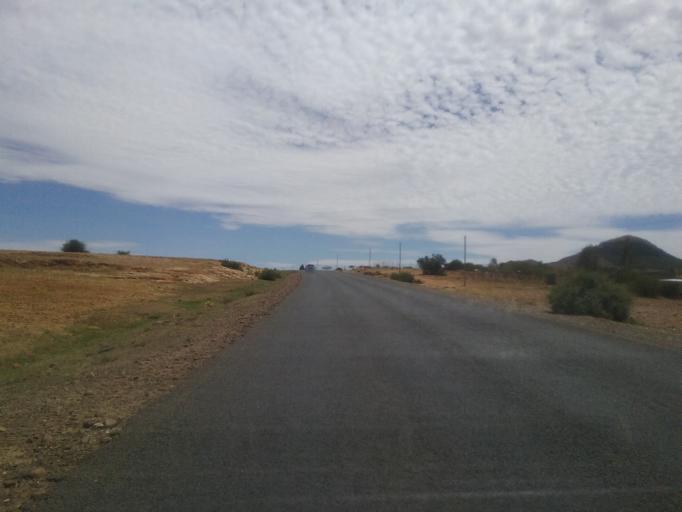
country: LS
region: Mafeteng
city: Mafeteng
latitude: -29.8625
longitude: 27.2360
